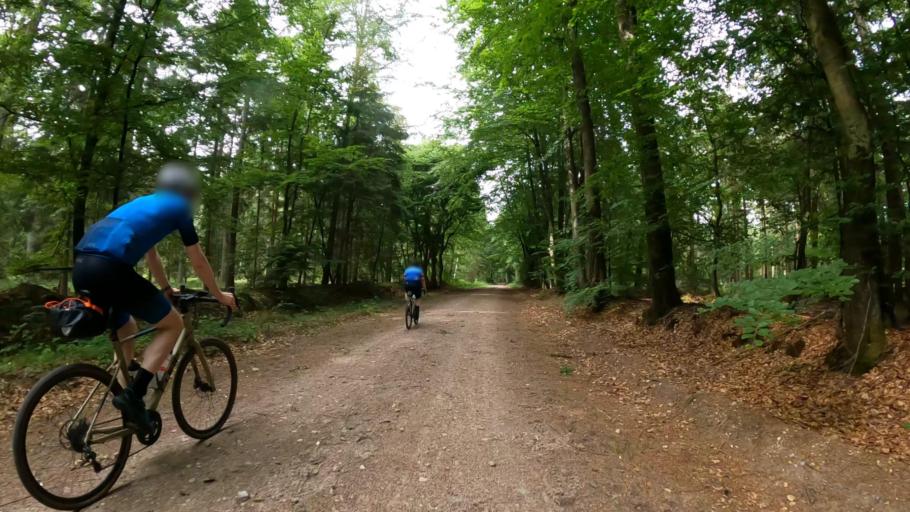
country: DE
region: Schleswig-Holstein
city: Heidmuhlen
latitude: 53.9556
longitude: 10.1179
